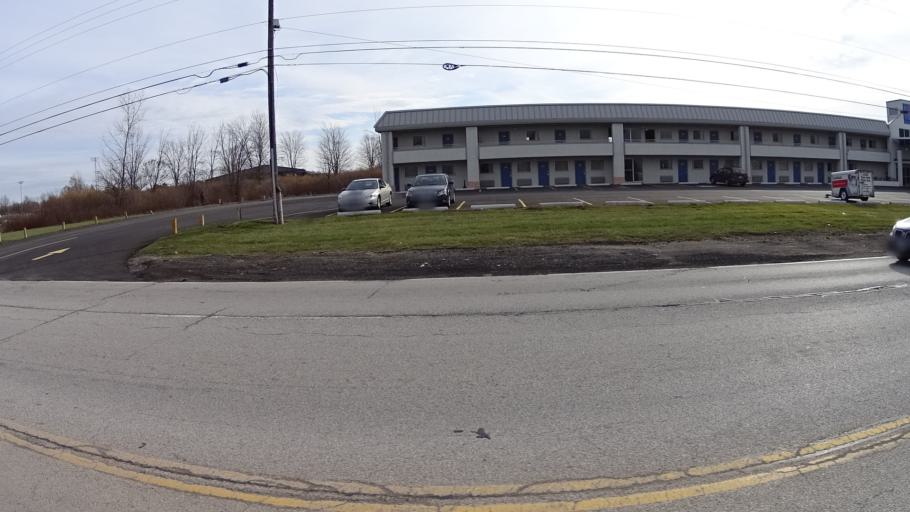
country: US
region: Ohio
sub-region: Lorain County
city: North Ridgeville
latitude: 41.3828
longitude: -81.9801
